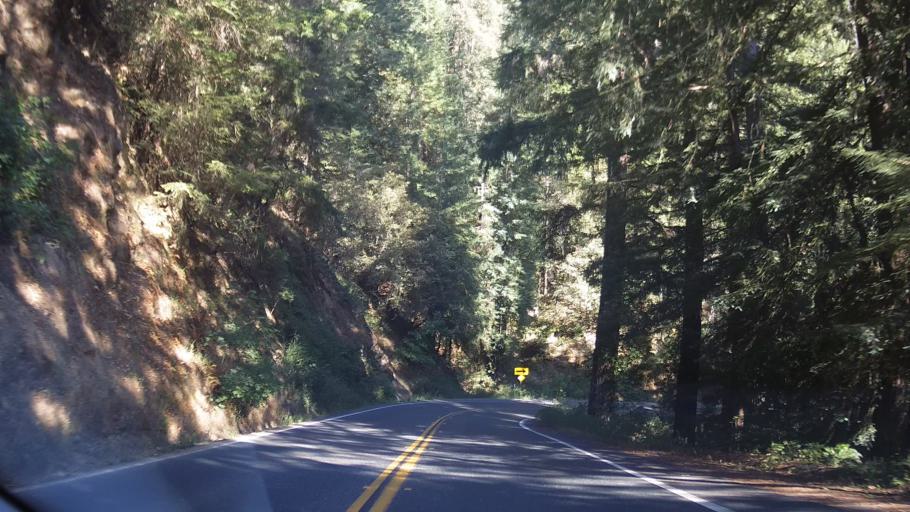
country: US
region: California
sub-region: Mendocino County
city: Brooktrails
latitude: 39.3691
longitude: -123.4967
